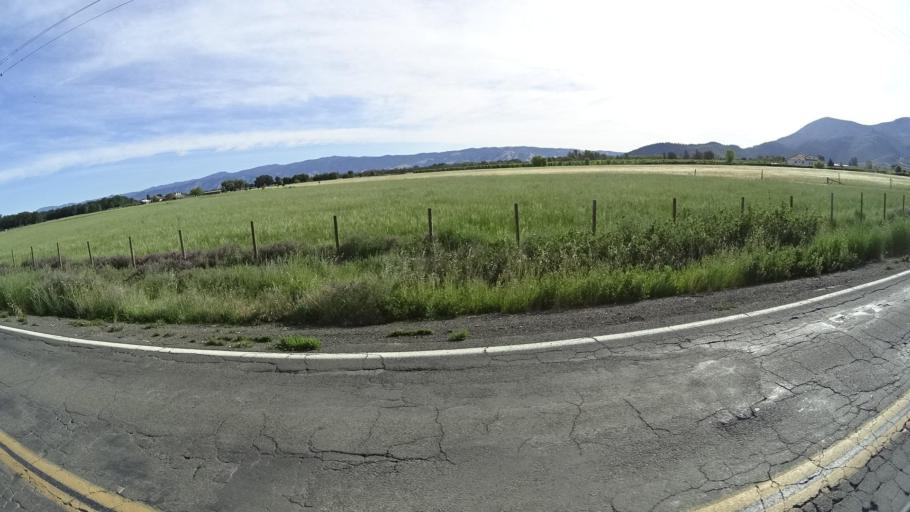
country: US
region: California
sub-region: Lake County
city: Kelseyville
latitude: 38.9901
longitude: -122.8563
